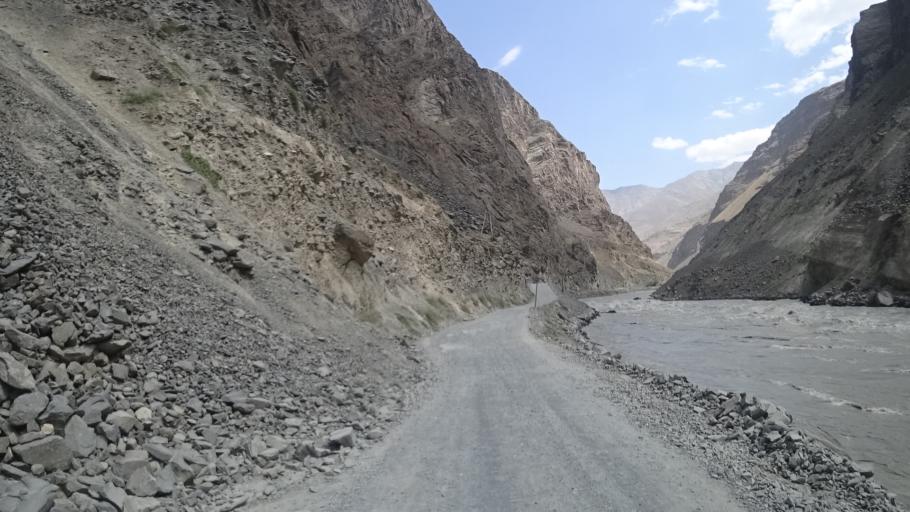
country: AF
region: Badakhshan
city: Maymay
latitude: 38.3423
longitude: 71.2004
